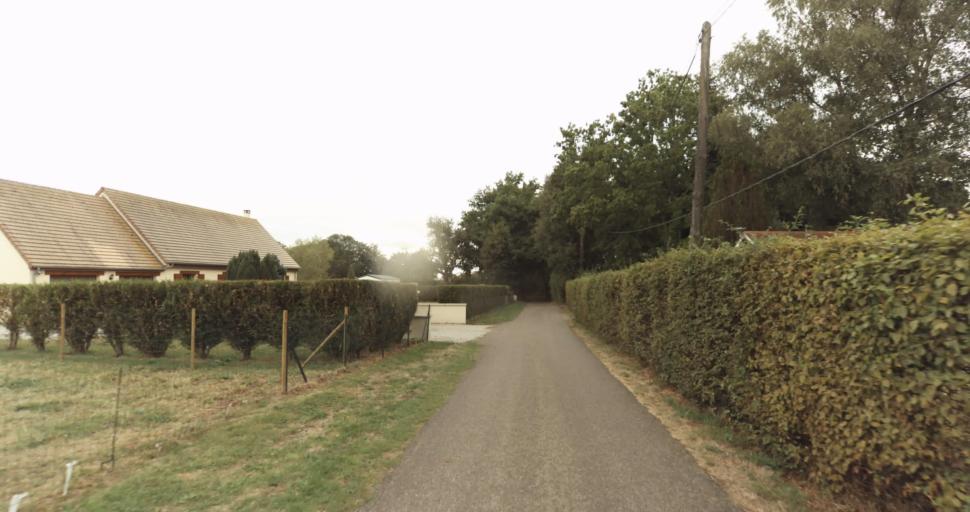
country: FR
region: Lower Normandy
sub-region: Departement de l'Orne
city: Gace
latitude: 48.8095
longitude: 0.3402
